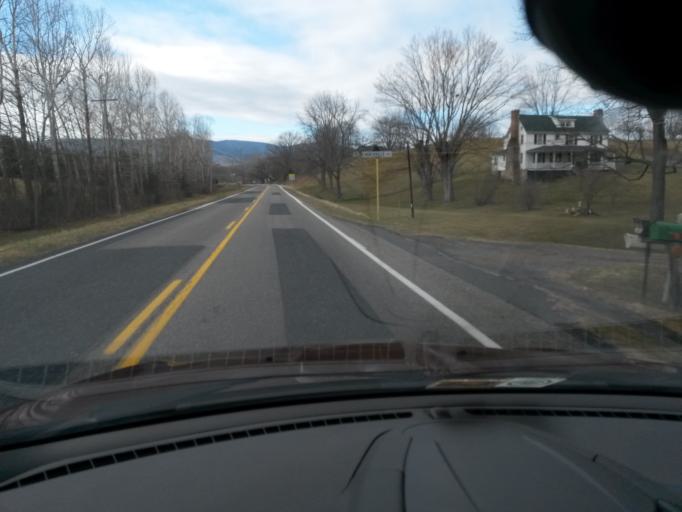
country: US
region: Virginia
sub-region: City of Staunton
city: Staunton
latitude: 38.2258
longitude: -79.1724
